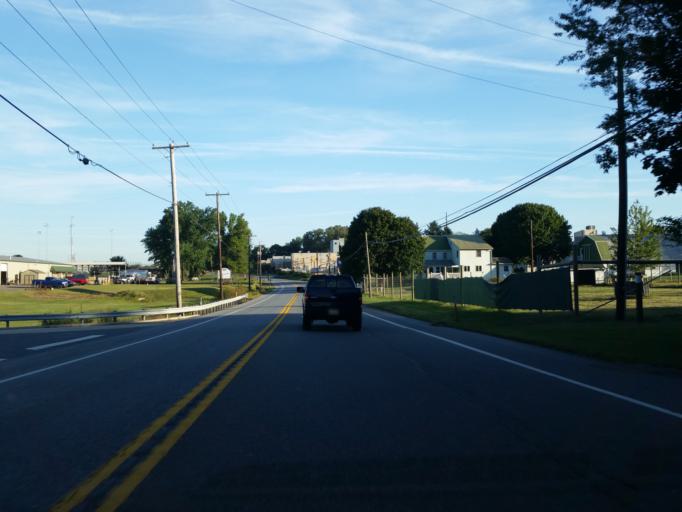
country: US
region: Pennsylvania
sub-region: Lancaster County
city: Quarryville
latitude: 39.8782
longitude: -76.2303
